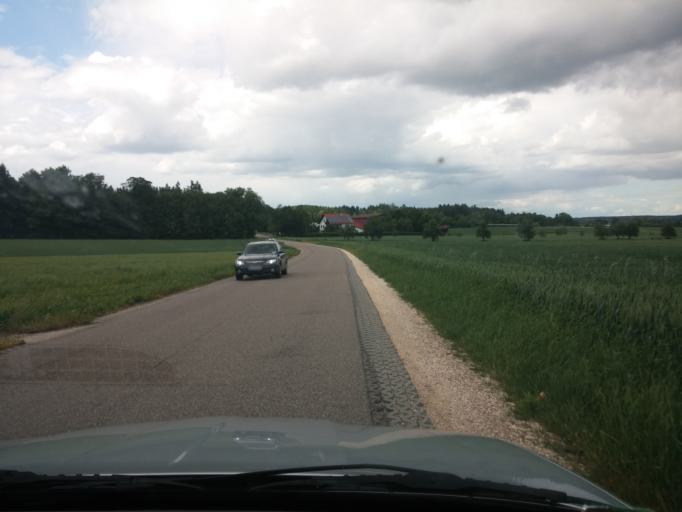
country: DE
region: Bavaria
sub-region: Swabia
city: Illertissen
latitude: 48.2268
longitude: 10.1189
